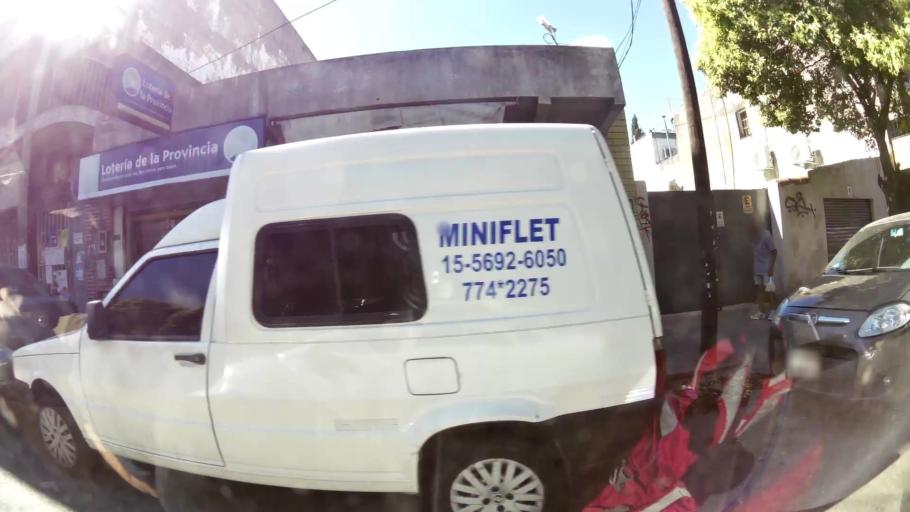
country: AR
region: Buenos Aires
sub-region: Partido de General San Martin
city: General San Martin
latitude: -34.5370
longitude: -58.5105
